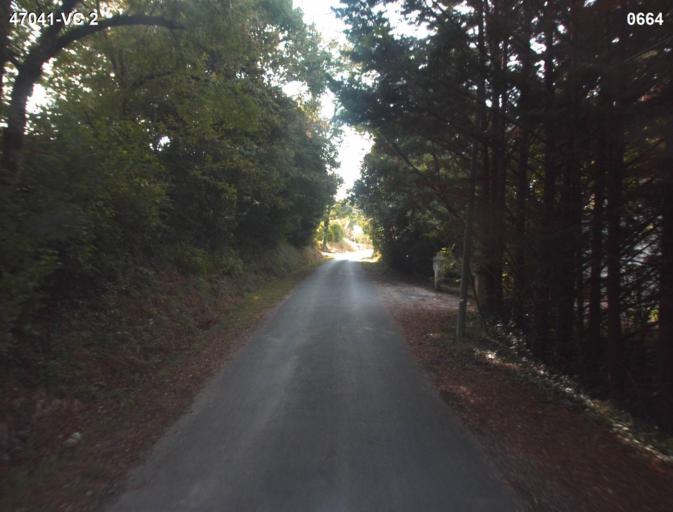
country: FR
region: Aquitaine
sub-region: Departement du Lot-et-Garonne
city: Port-Sainte-Marie
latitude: 44.1963
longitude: 0.4110
